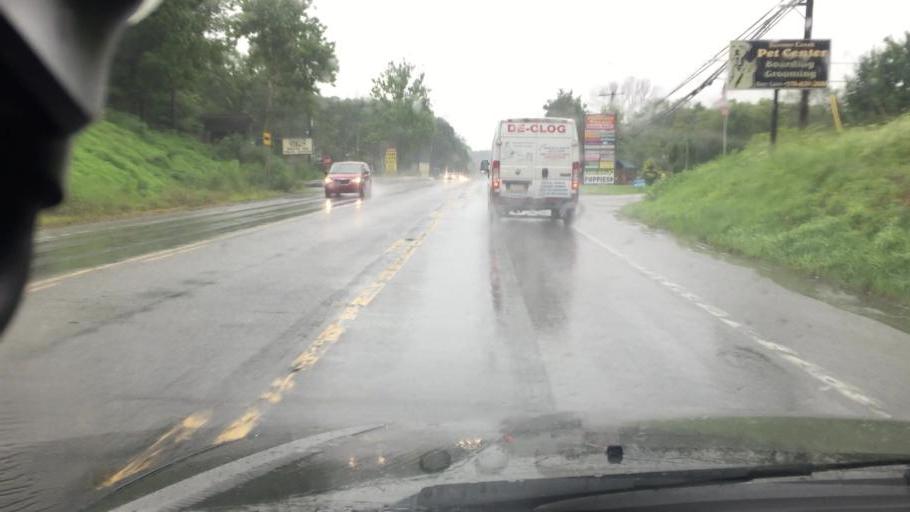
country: US
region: Pennsylvania
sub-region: Monroe County
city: Tannersville
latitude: 41.0254
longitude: -75.2990
